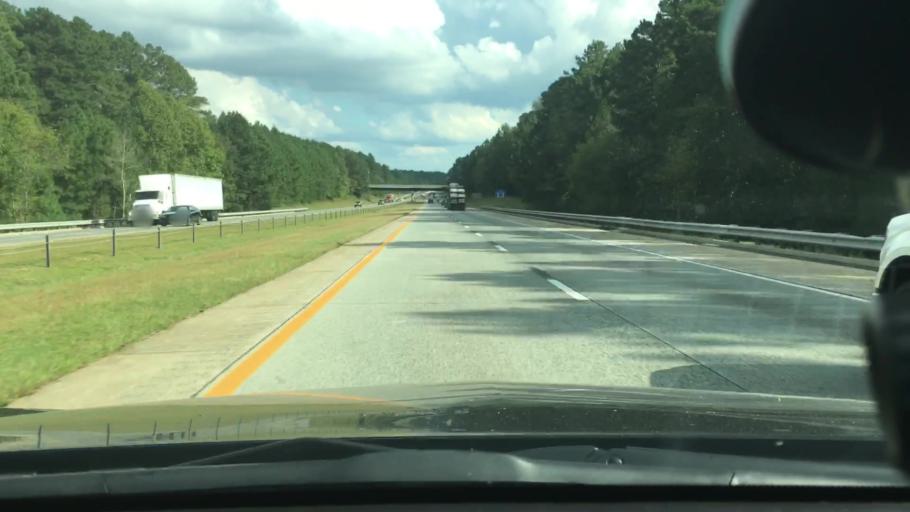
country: US
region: North Carolina
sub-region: Orange County
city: Chapel Hill
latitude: 35.9620
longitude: -79.0165
